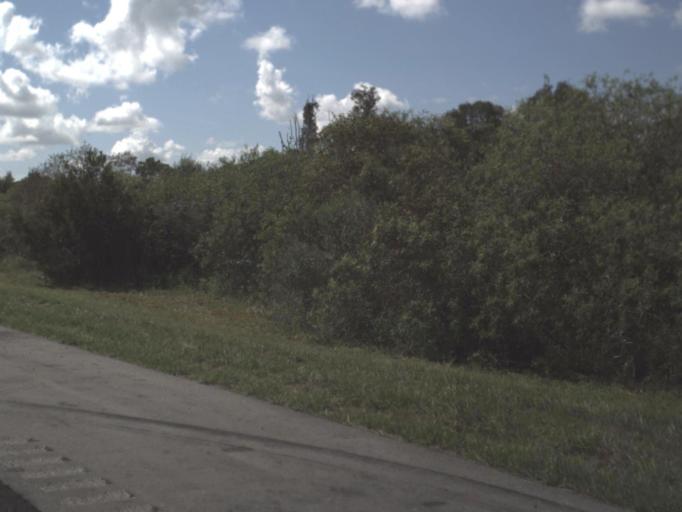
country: US
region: Florida
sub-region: Lee County
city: Suncoast Estates
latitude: 26.7475
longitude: -81.8597
